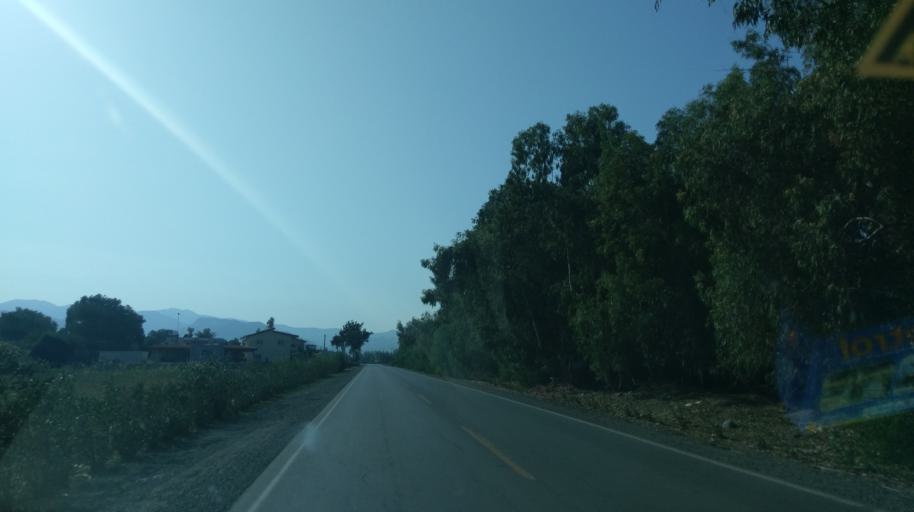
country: CY
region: Lefkosia
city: Lefka
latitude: 35.1532
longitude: 32.8637
